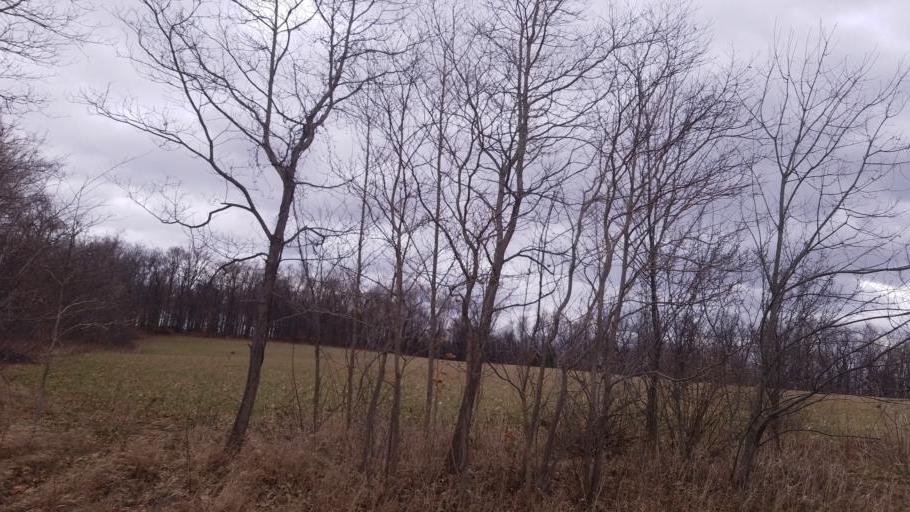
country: US
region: Ohio
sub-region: Licking County
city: Utica
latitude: 40.2214
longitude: -82.3909
